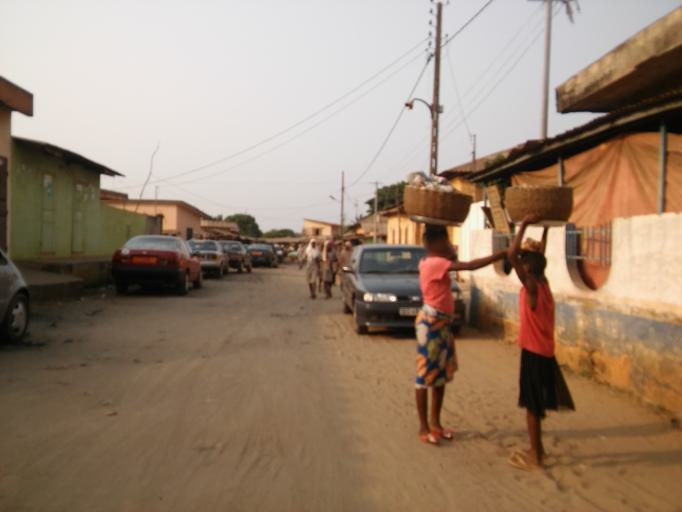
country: BJ
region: Queme
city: Porto-Novo
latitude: 6.4778
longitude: 2.6224
